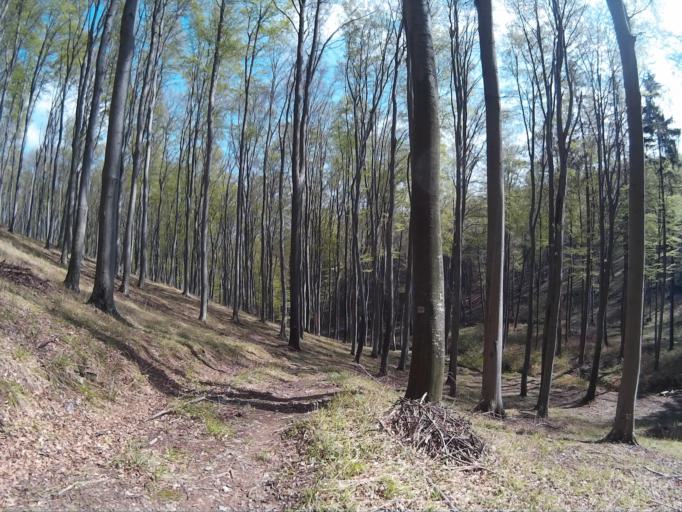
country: AT
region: Burgenland
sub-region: Politischer Bezirk Oberwart
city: Rechnitz
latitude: 47.3486
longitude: 16.4513
